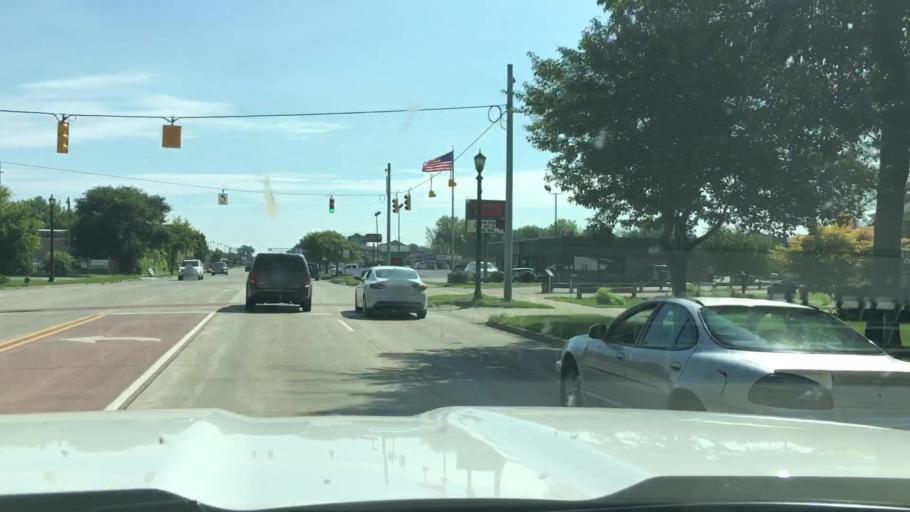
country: US
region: Michigan
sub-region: Bay County
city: Essexville
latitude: 43.5954
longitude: -83.8550
